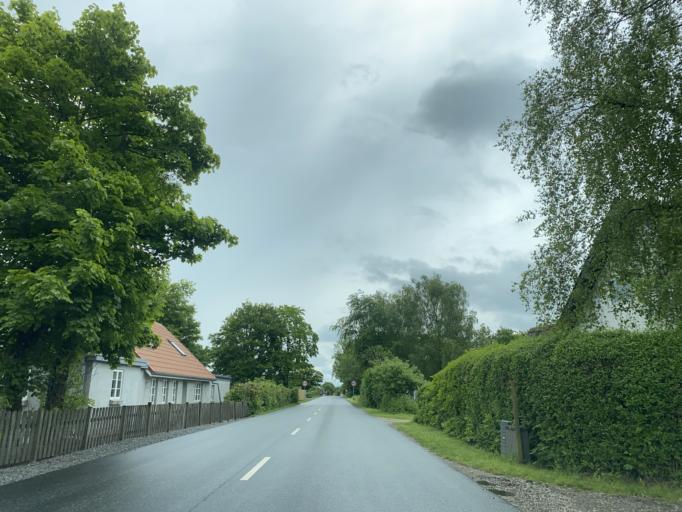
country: DK
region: Central Jutland
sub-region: Arhus Kommune
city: Sabro
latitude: 56.2559
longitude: 9.9612
